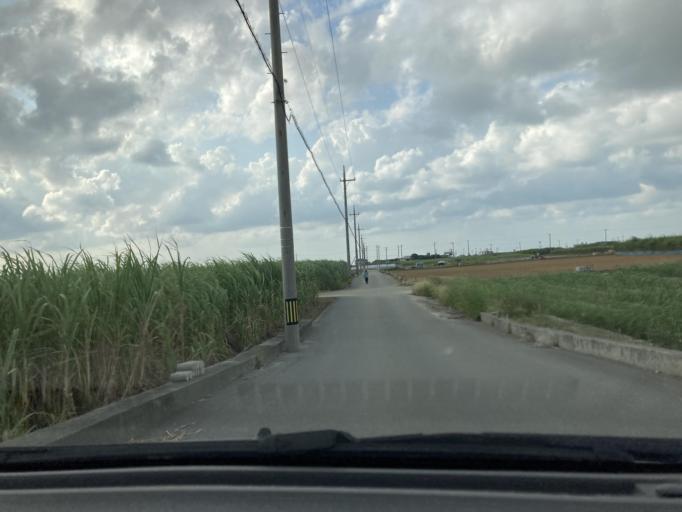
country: JP
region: Okinawa
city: Itoman
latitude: 26.0828
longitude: 127.6683
